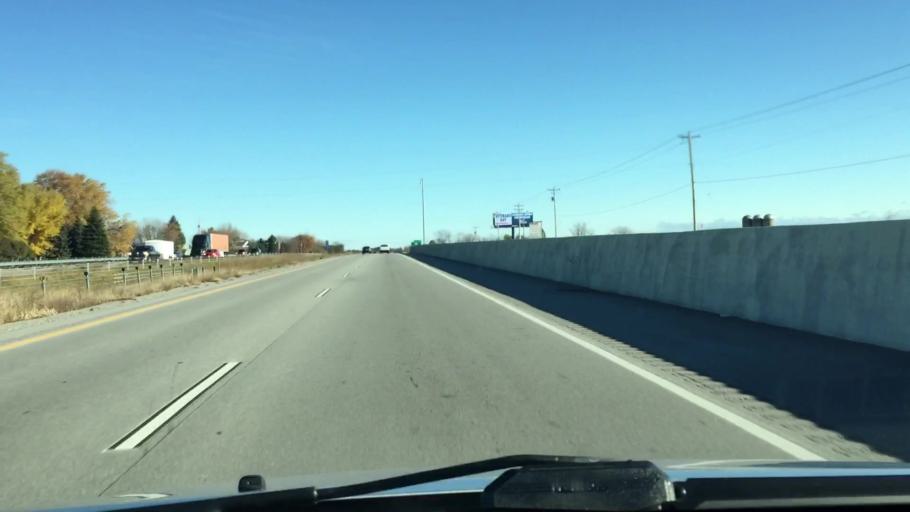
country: US
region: Wisconsin
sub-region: Brown County
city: Wrightstown
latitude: 44.3669
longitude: -88.1775
